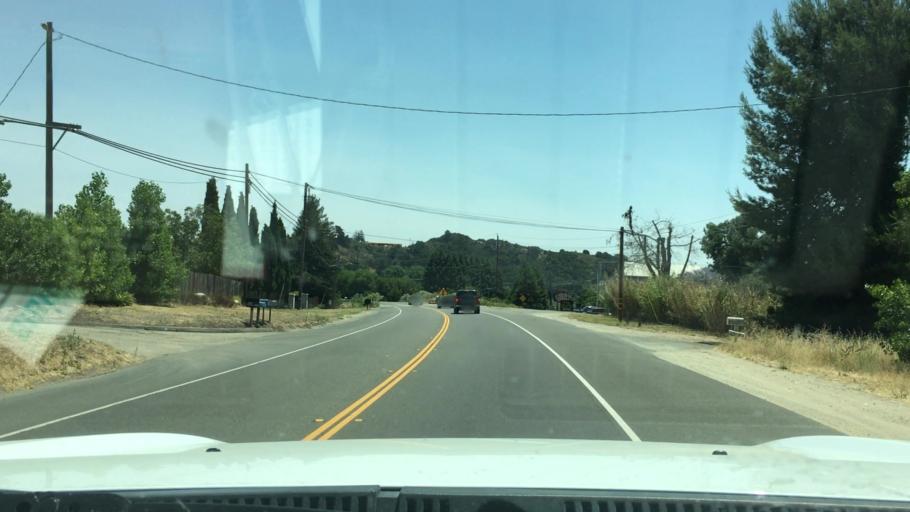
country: US
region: California
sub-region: San Luis Obispo County
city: Pismo Beach
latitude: 35.2035
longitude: -120.6127
